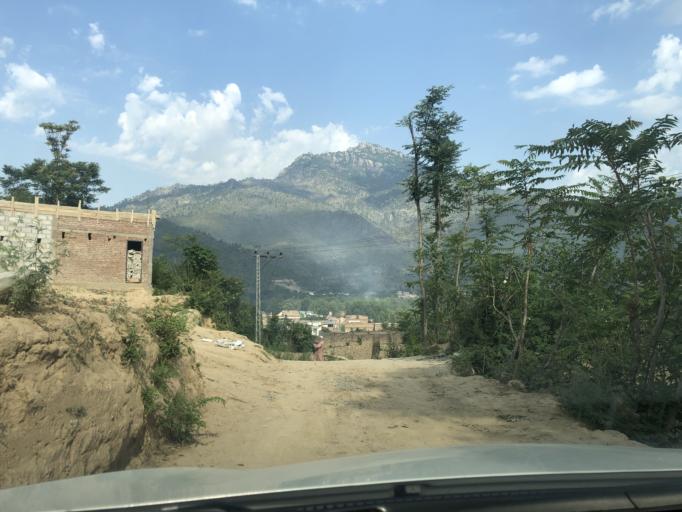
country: PK
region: Khyber Pakhtunkhwa
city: Daggar
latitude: 34.5934
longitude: 72.4540
